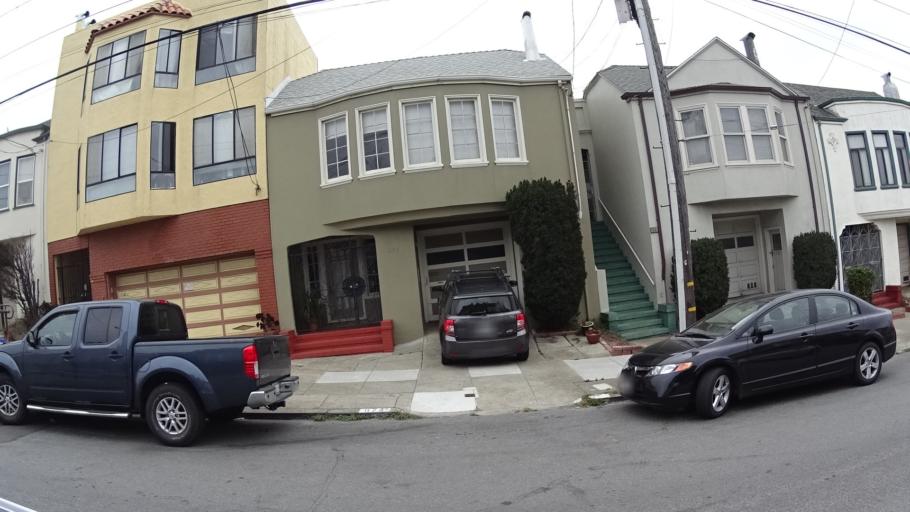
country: US
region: California
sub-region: San Francisco County
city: San Francisco
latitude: 37.7762
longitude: -122.4974
